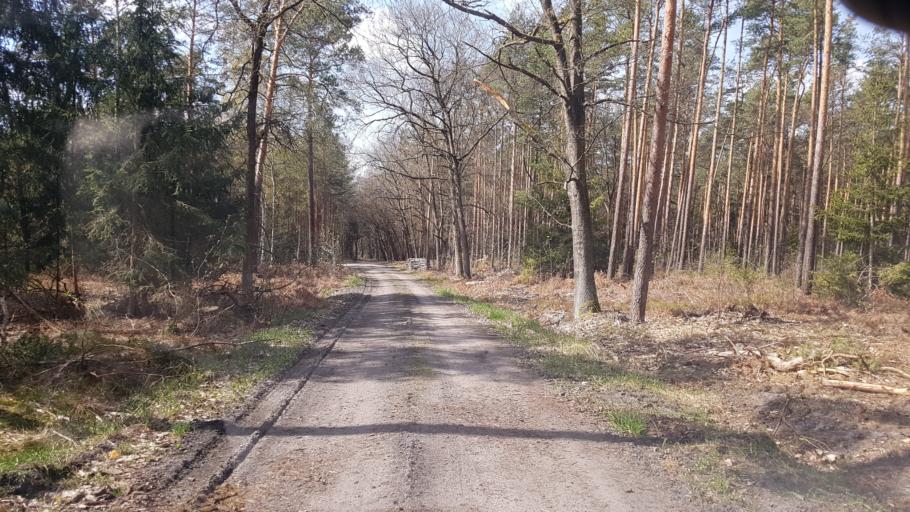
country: DE
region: Brandenburg
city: Ruckersdorf
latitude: 51.5495
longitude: 13.6469
